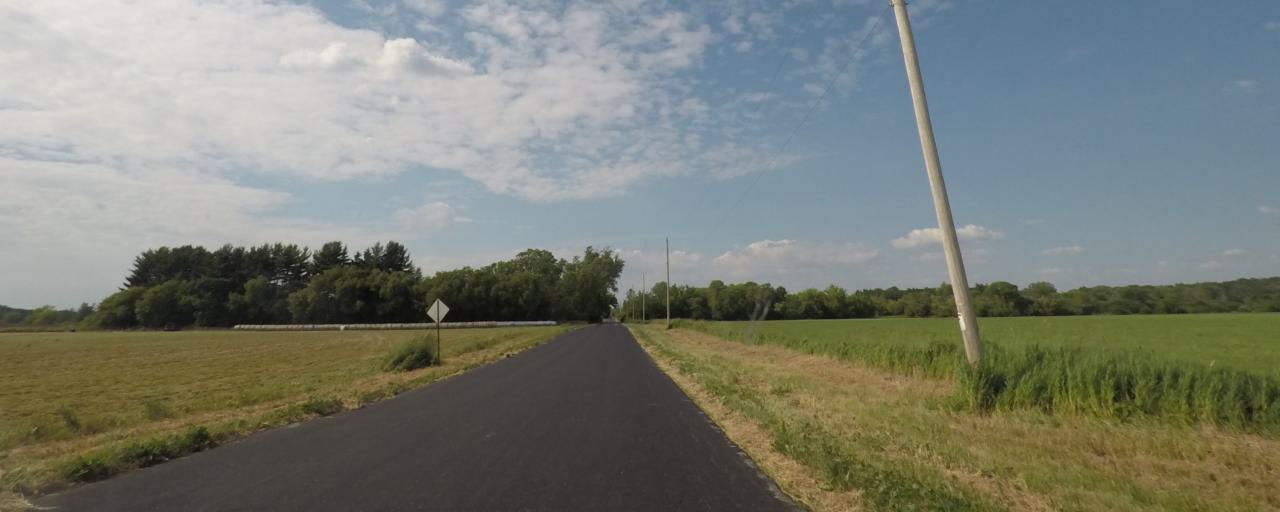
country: US
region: Wisconsin
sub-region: Walworth County
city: Elkhorn
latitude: 42.7802
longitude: -88.5294
